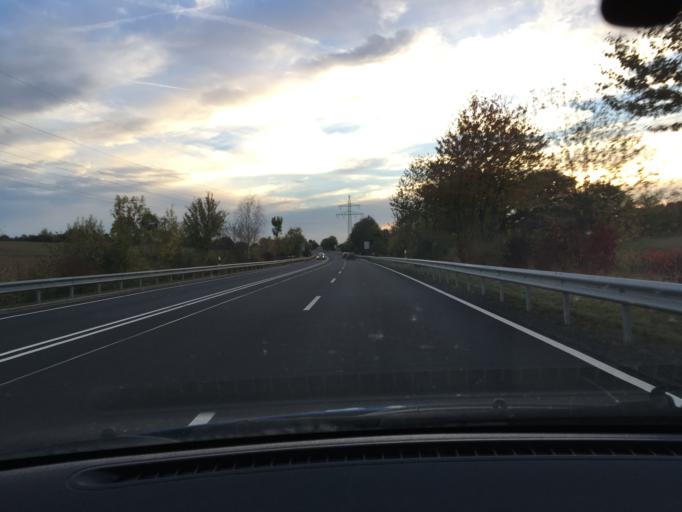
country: DE
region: Lower Saxony
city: Hardegsen
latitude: 51.6419
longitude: 9.8100
